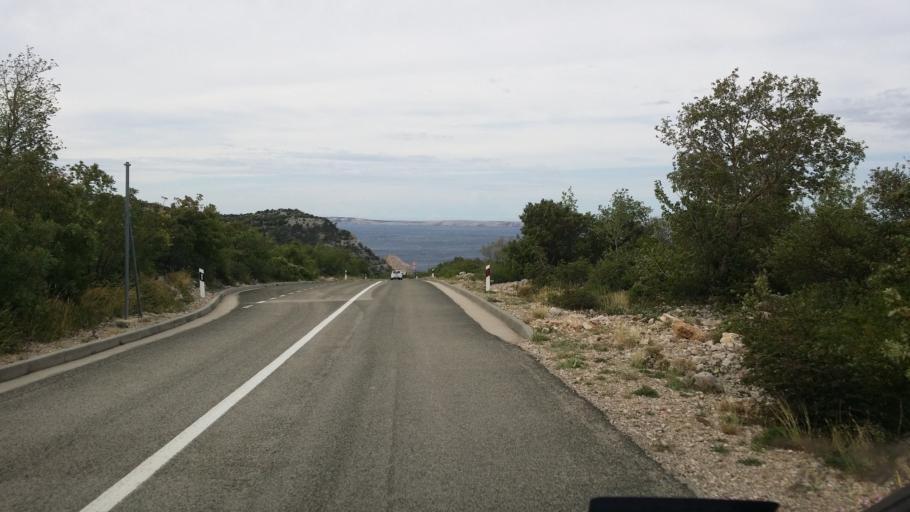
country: HR
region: Primorsko-Goranska
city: Banjol
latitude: 44.7110
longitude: 14.9008
